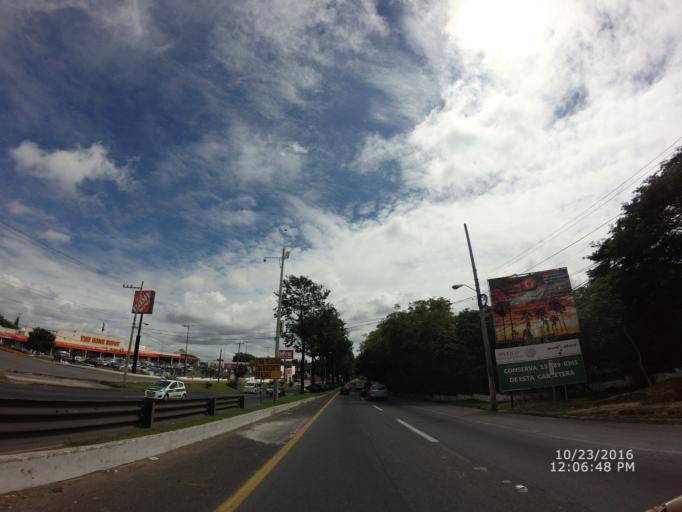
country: MX
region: Veracruz
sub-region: Xalapa
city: Lomas Verdes
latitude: 19.5216
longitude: -96.8904
